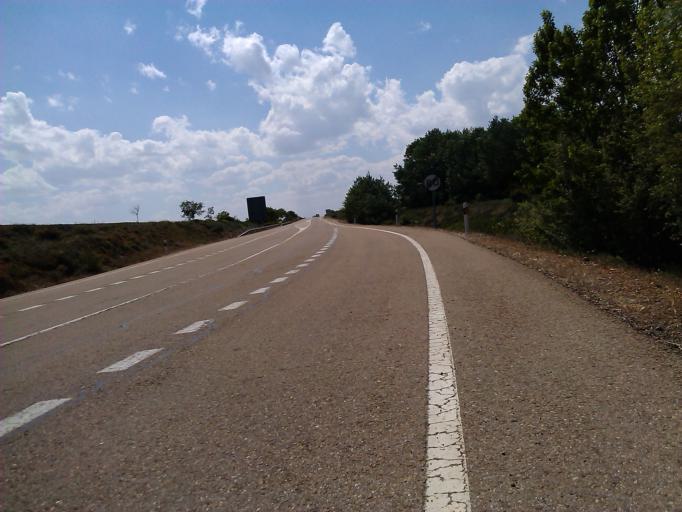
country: ES
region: Castille and Leon
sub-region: Provincia de Palencia
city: Ledigos
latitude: 42.3662
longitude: -4.8754
